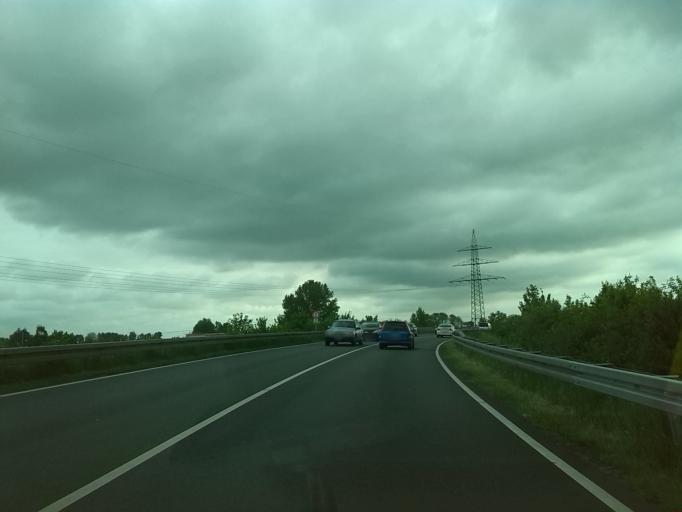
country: DE
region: Hesse
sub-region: Regierungsbezirk Darmstadt
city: Erzhausen
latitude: 49.9192
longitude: 8.6451
